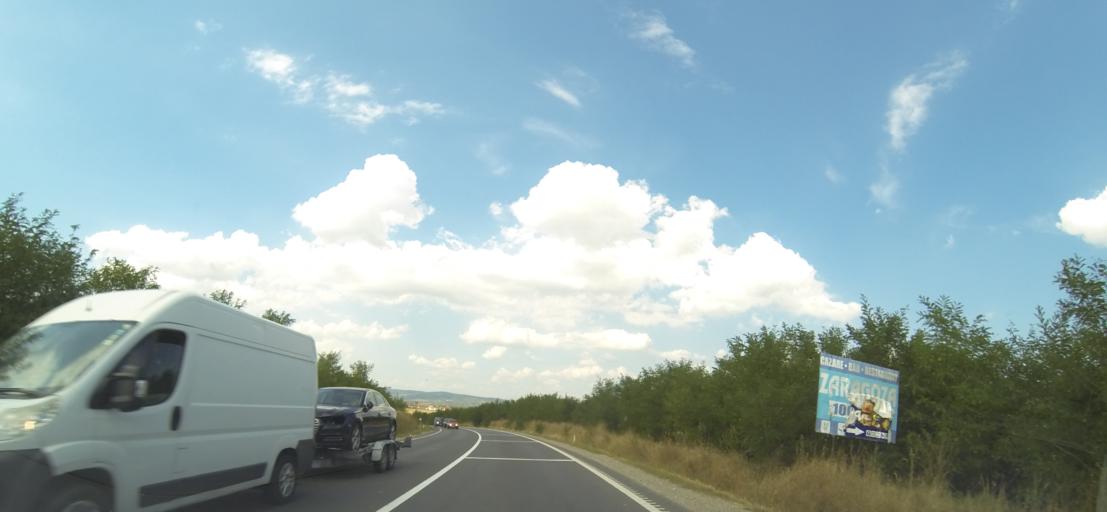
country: RO
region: Brasov
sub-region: Comuna Sercaia
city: Sercaia
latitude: 45.8224
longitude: 25.1578
